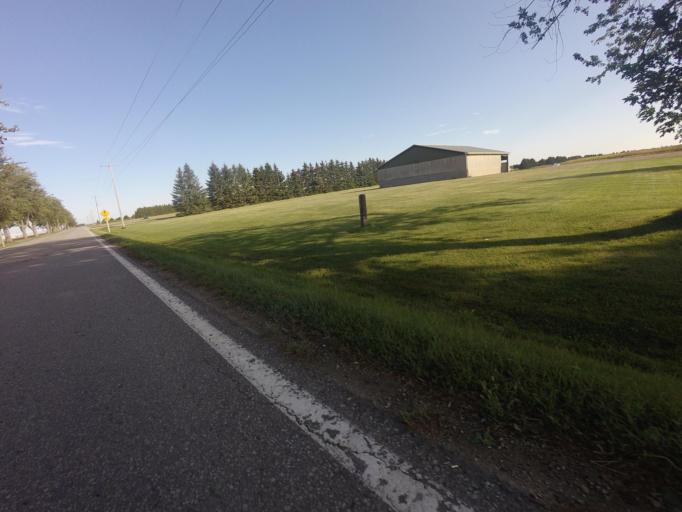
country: CA
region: Ontario
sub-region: Wellington County
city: Guelph
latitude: 43.6396
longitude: -80.4005
